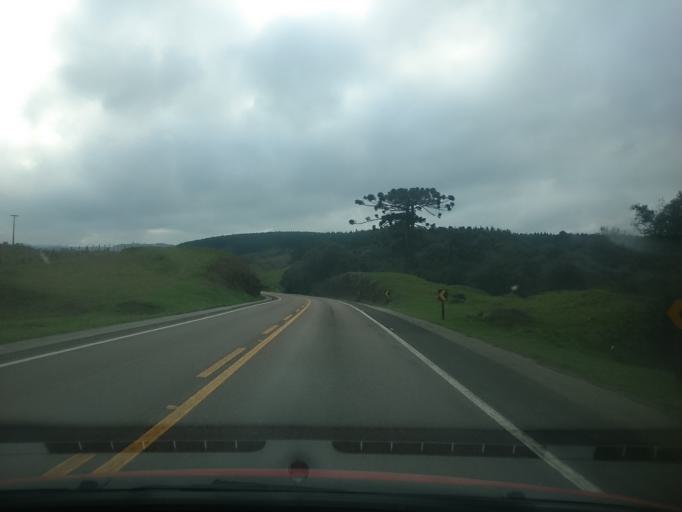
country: BR
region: Santa Catarina
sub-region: Lages
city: Lages
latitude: -27.8820
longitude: -50.4116
